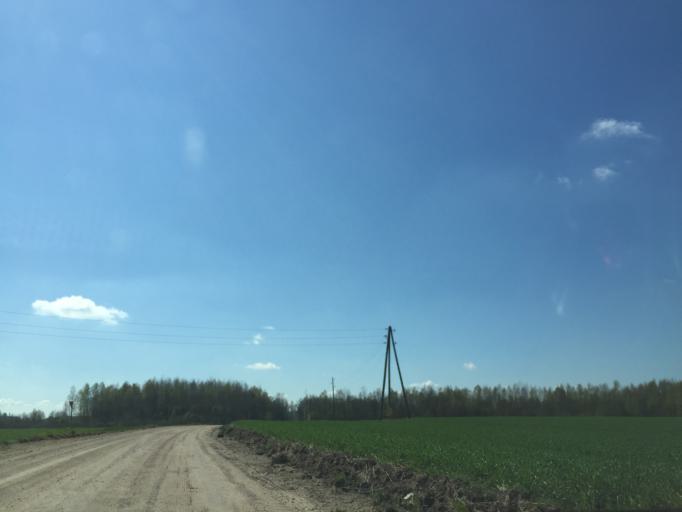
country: LV
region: Smiltene
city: Smiltene
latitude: 57.5641
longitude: 25.9050
